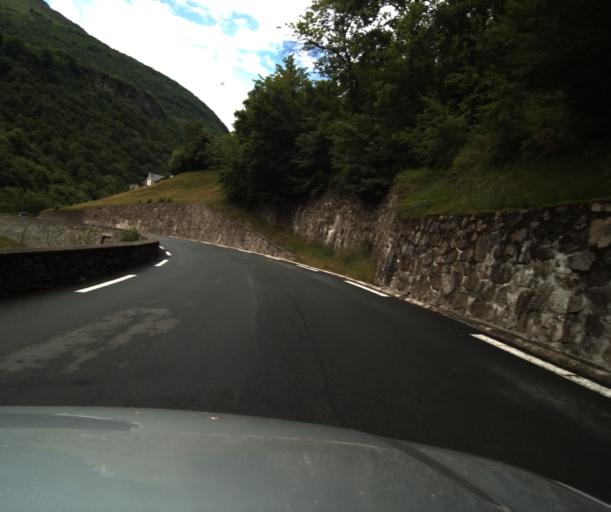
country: FR
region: Midi-Pyrenees
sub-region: Departement des Hautes-Pyrenees
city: Luz-Saint-Sauveur
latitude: 42.7958
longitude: 0.0176
